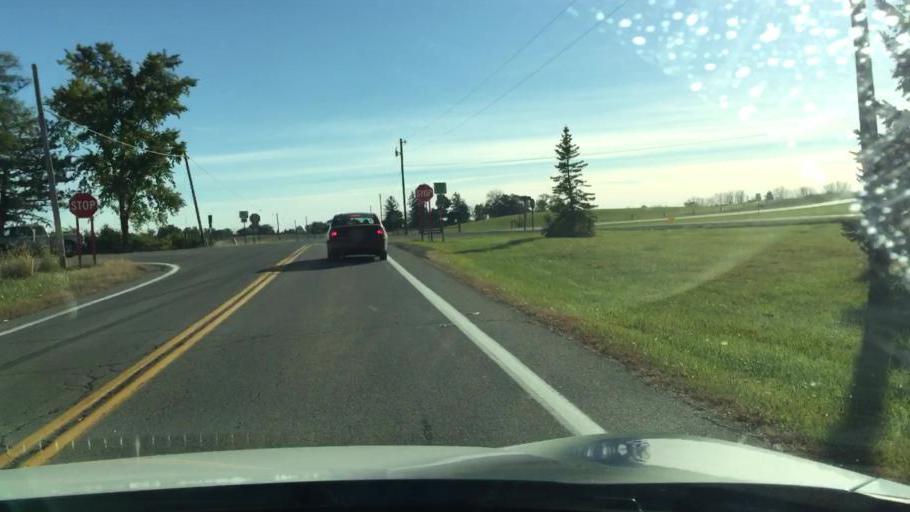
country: US
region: Ohio
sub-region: Champaign County
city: Mechanicsburg
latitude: 40.1016
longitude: -83.5429
